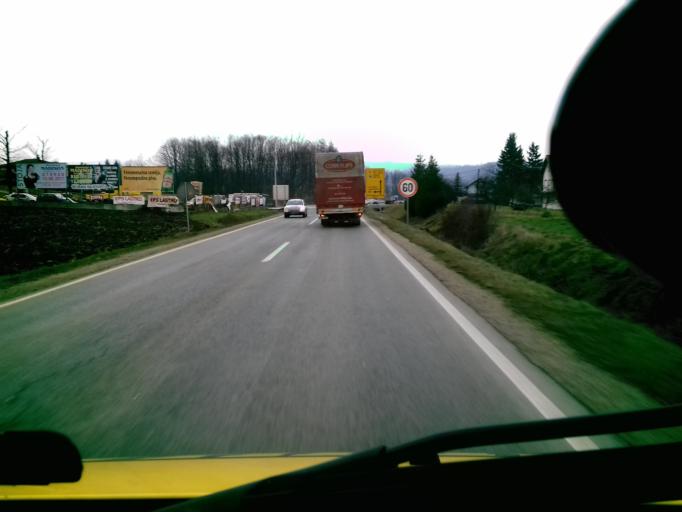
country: BA
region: Federation of Bosnia and Herzegovina
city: Lijesnica
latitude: 44.4761
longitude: 18.0686
